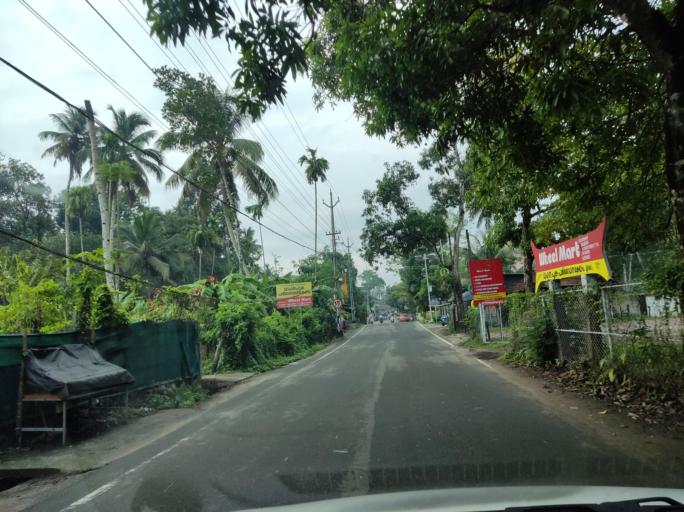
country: IN
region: Kerala
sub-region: Alappuzha
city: Kayankulam
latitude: 9.2150
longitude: 76.4616
